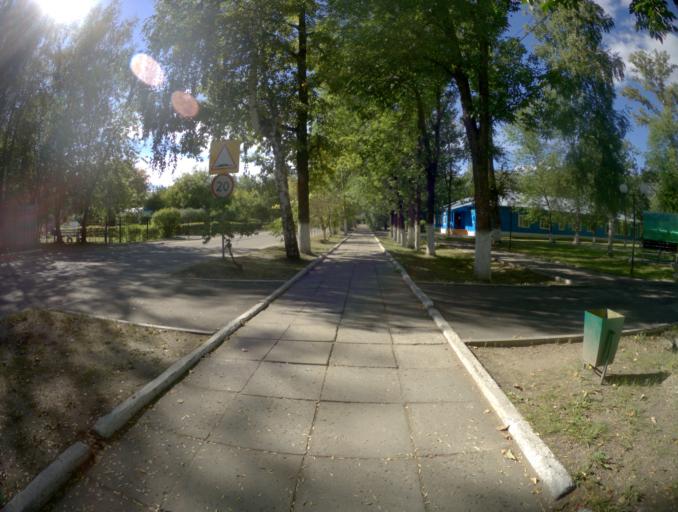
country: RU
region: Vladimir
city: Krasnaya Gorbatka
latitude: 55.8655
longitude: 41.7615
